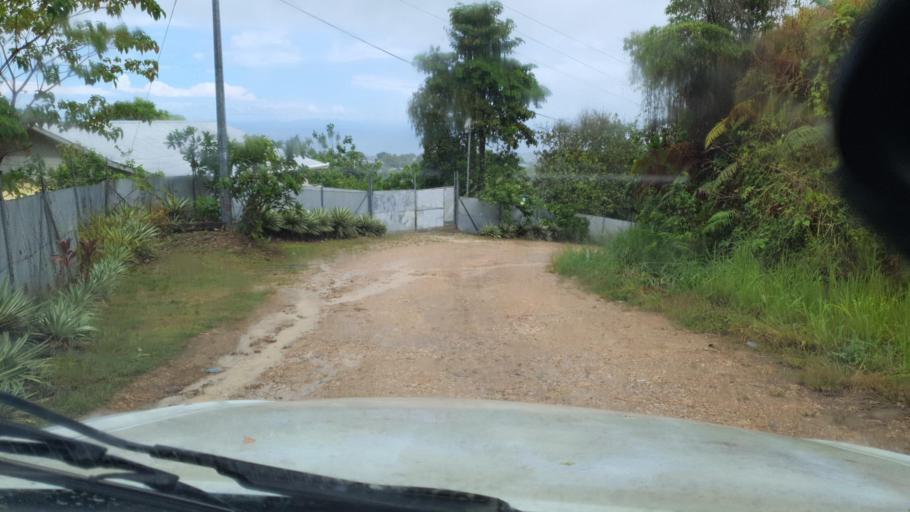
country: SB
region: Guadalcanal
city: Honiara
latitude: -9.4467
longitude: 159.9183
